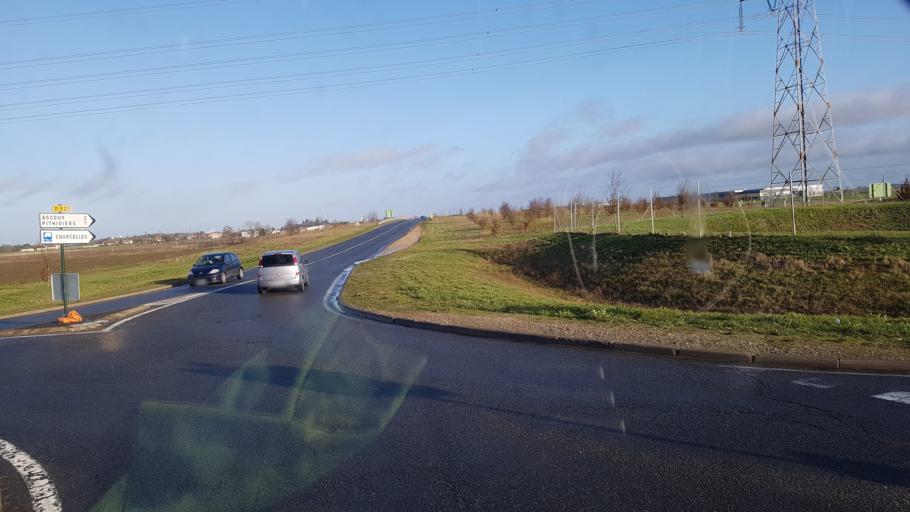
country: FR
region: Centre
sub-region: Departement du Loiret
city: Dadonville
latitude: 48.1108
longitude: 2.2478
